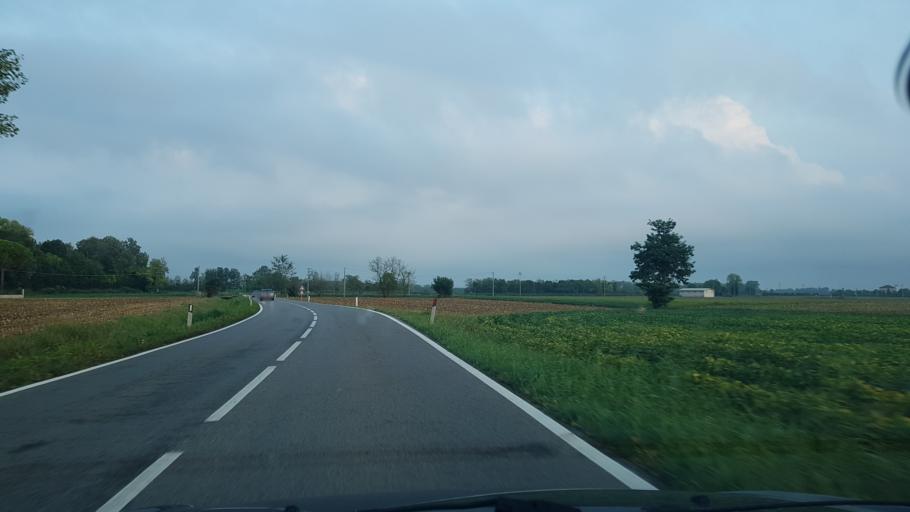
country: IT
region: Friuli Venezia Giulia
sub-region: Provincia di Udine
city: Trivignano Udinese
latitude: 45.9381
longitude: 13.3599
